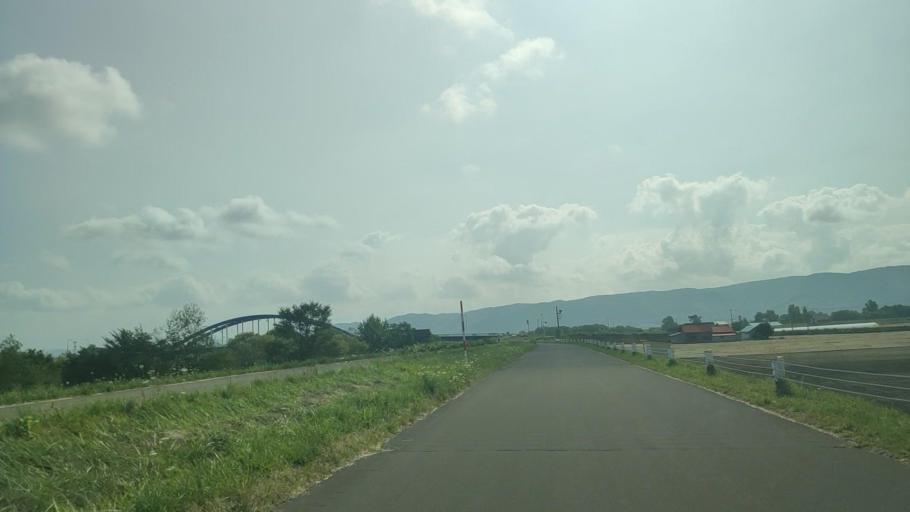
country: JP
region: Hokkaido
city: Shimo-furano
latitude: 43.3372
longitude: 142.3806
